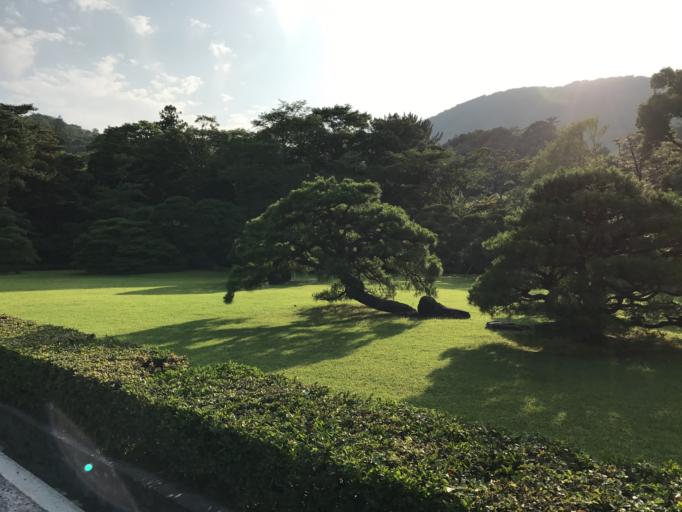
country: JP
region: Mie
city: Ise
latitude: 34.4576
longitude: 136.7232
